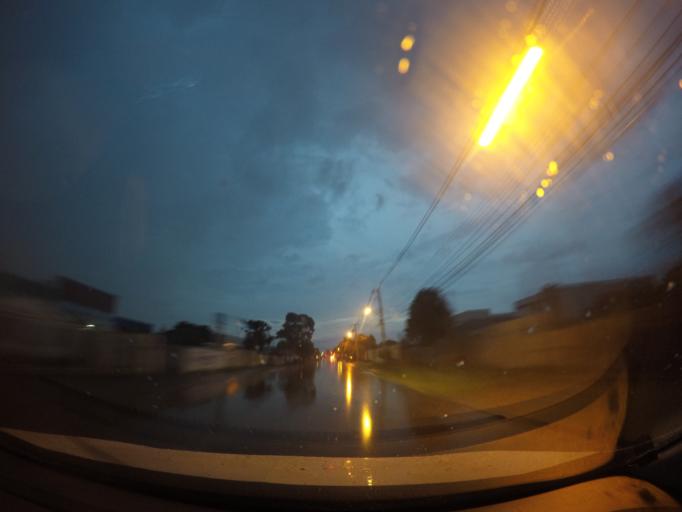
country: BR
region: Parana
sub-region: Sao Jose Dos Pinhais
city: Sao Jose dos Pinhais
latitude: -25.4973
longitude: -49.2356
